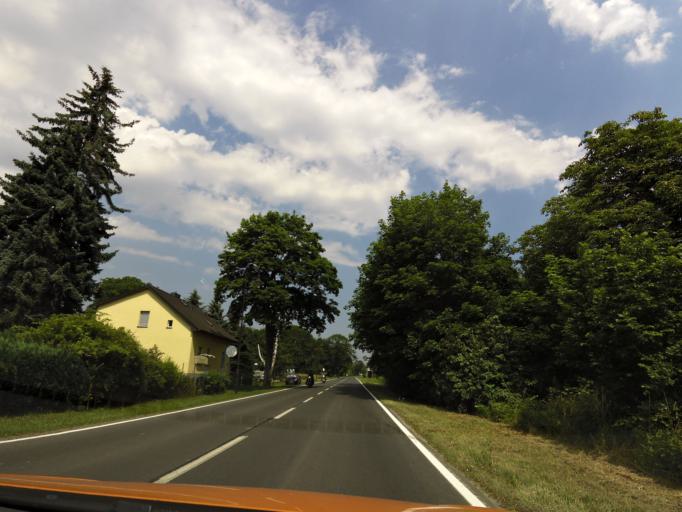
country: DE
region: Brandenburg
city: Wustermark
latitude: 52.5299
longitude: 12.9317
